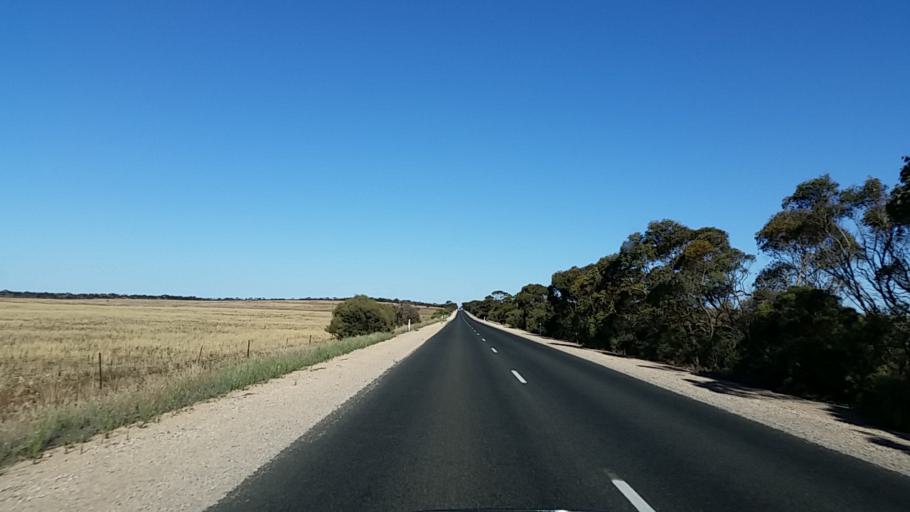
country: AU
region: South Australia
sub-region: Mid Murray
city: Mannum
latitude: -34.7572
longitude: 139.5046
